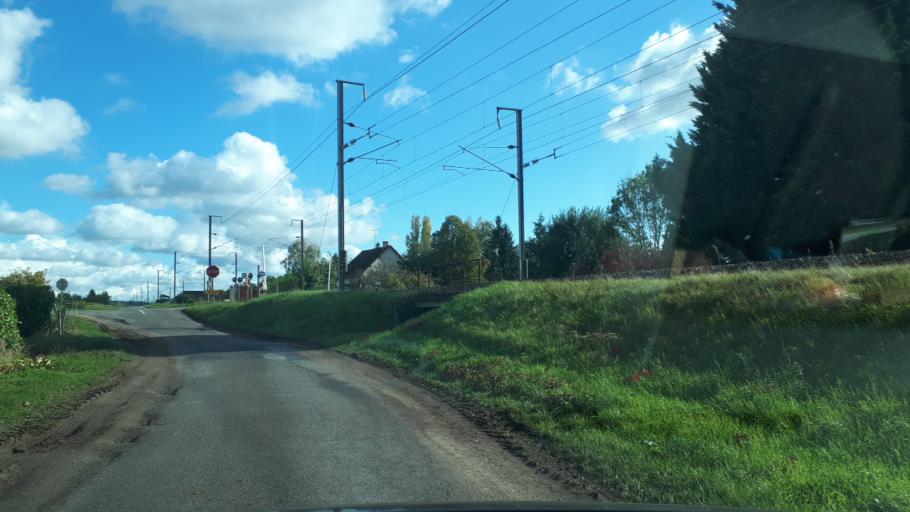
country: FR
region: Centre
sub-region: Departement du Loir-et-Cher
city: Thesee
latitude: 47.3194
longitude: 1.3215
